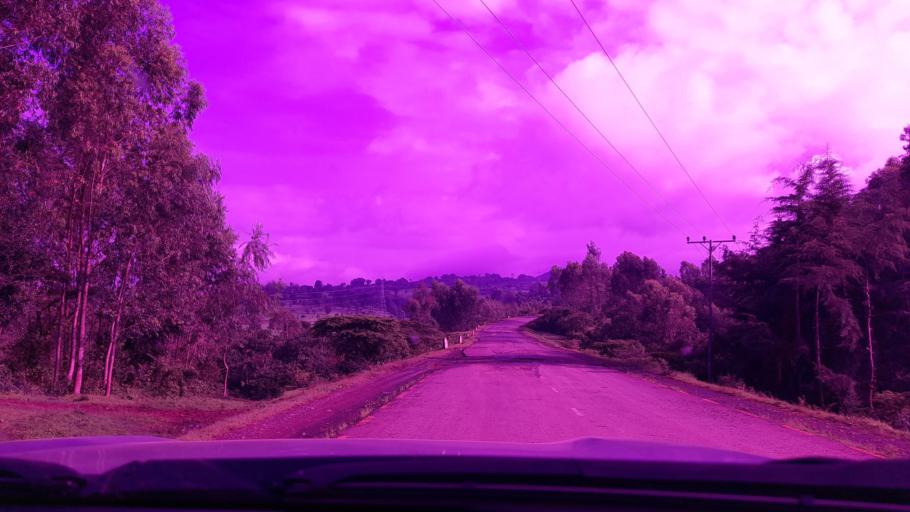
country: ET
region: Oromiya
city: Bedele
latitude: 8.2154
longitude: 36.4449
